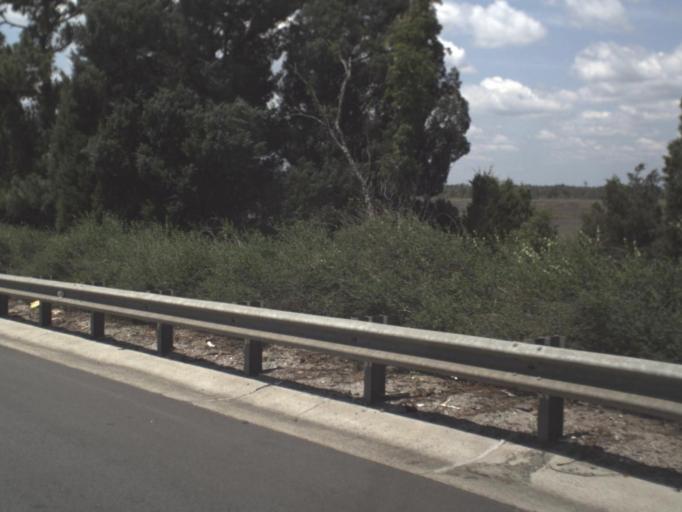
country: US
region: Georgia
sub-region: Camden County
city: Kingsland
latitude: 30.7414
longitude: -81.6559
